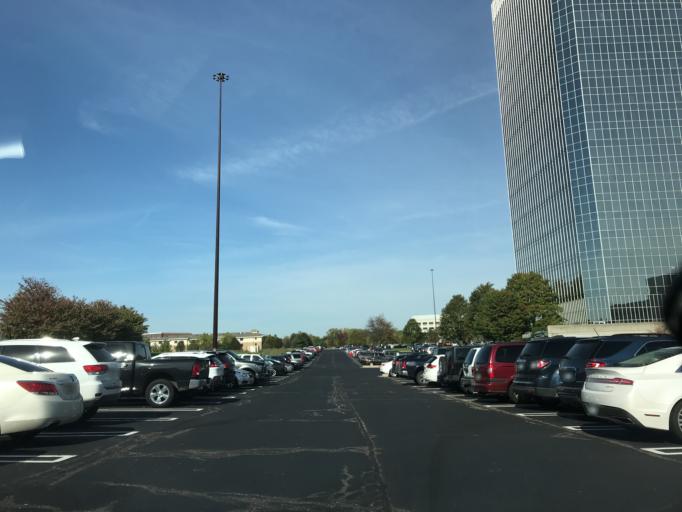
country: US
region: Michigan
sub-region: Oakland County
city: Franklin
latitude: 42.4886
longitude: -83.2990
